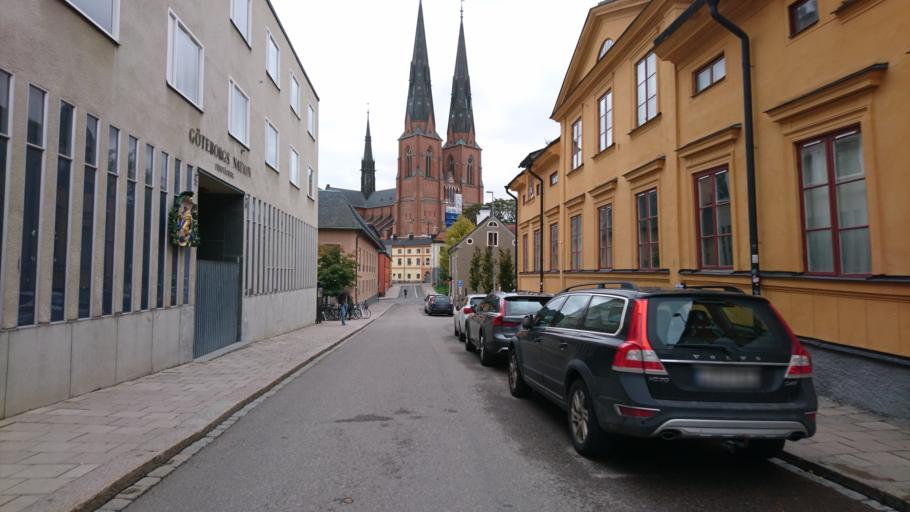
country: SE
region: Uppsala
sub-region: Uppsala Kommun
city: Uppsala
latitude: 59.8595
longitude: 17.6298
